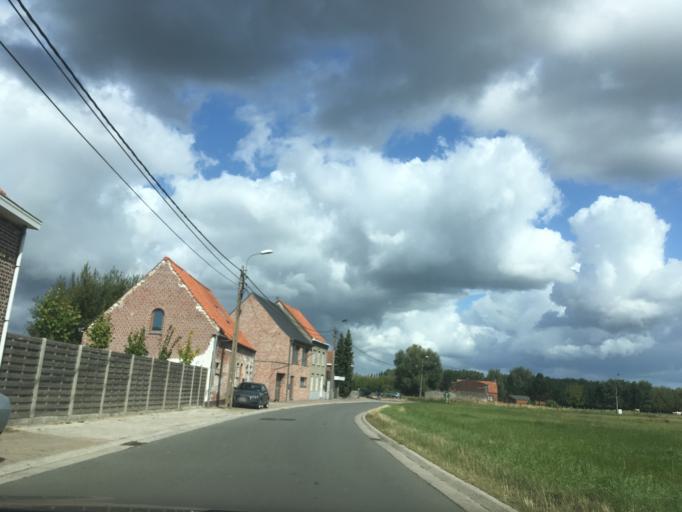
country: BE
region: Flanders
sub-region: Provincie West-Vlaanderen
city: Kortemark
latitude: 51.0199
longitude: 3.0333
